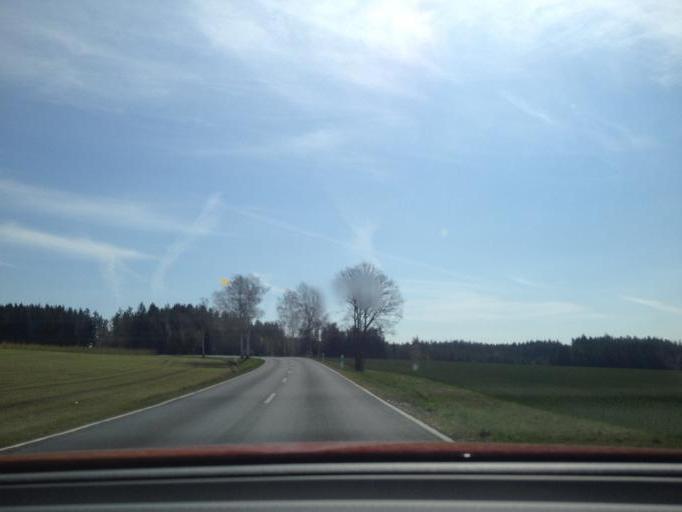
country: DE
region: Bavaria
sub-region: Upper Franconia
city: Roslau
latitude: 50.0766
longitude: 12.0189
